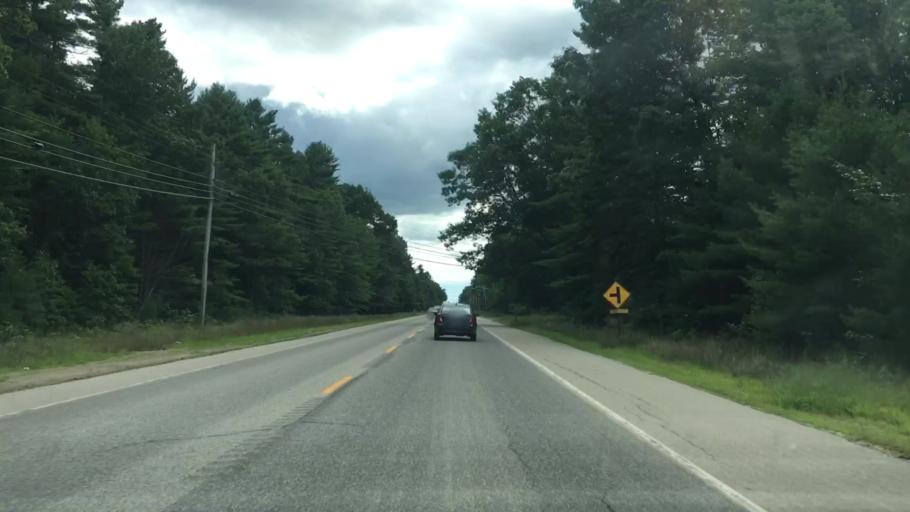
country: US
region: Maine
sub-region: York County
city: North Berwick
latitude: 43.3378
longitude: -70.7332
